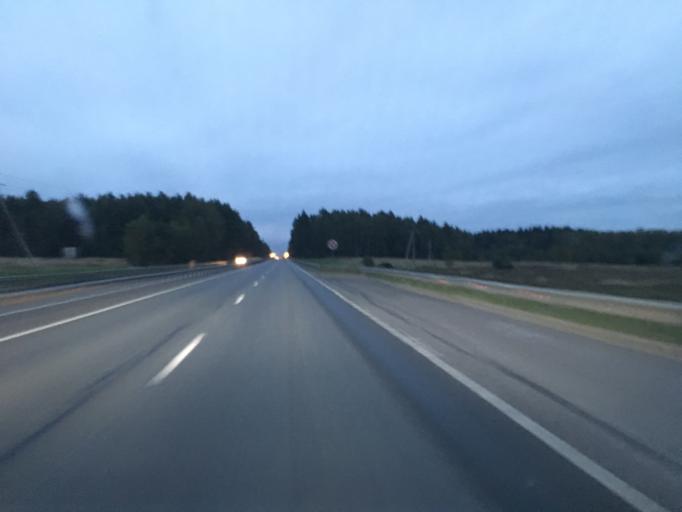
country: RU
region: Kaluga
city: Maloyaroslavets
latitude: 54.9680
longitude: 36.4750
